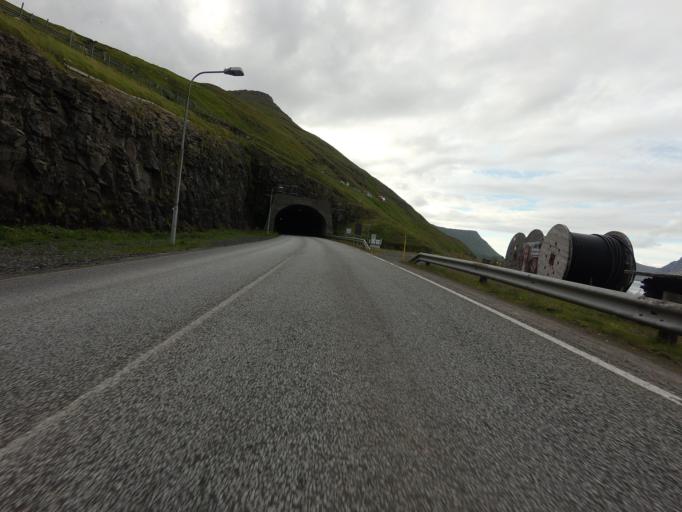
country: FO
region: Eysturoy
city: Eystur
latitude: 62.2147
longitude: -6.7176
